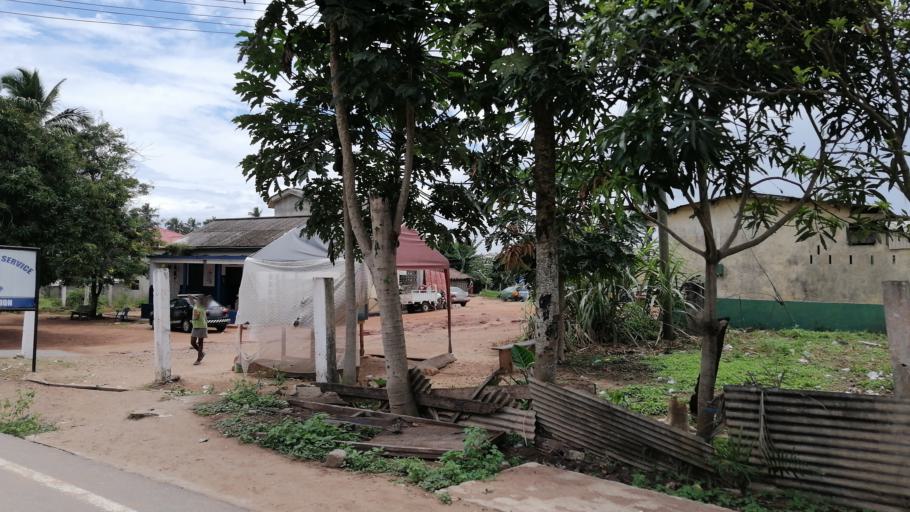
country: GH
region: Central
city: Elmina
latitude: 5.0920
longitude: -1.3459
